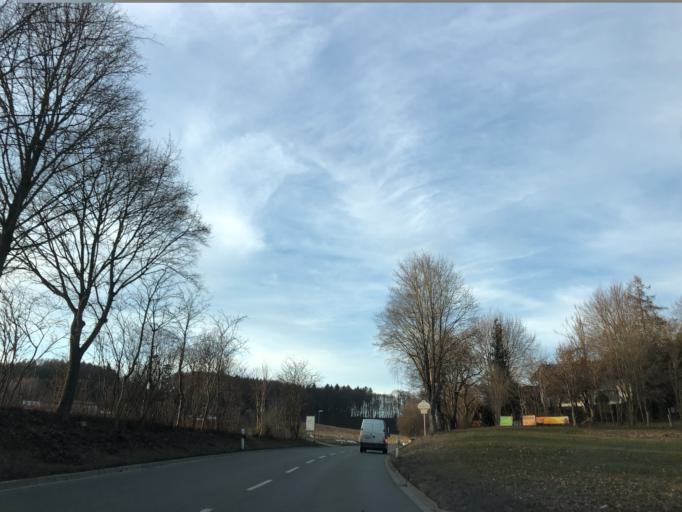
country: DE
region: Bavaria
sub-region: Upper Bavaria
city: Ebersberg
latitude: 48.0861
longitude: 11.9669
